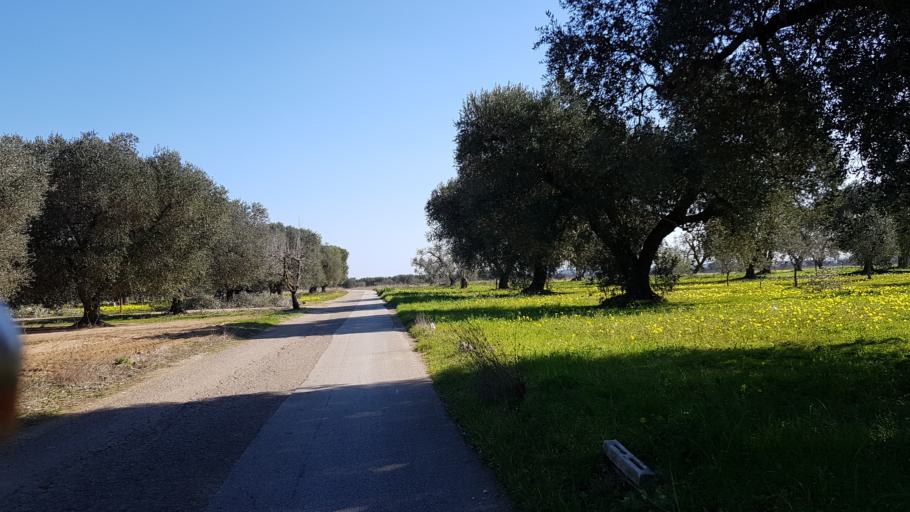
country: IT
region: Apulia
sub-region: Provincia di Brindisi
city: Mesagne
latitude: 40.6192
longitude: 17.8397
